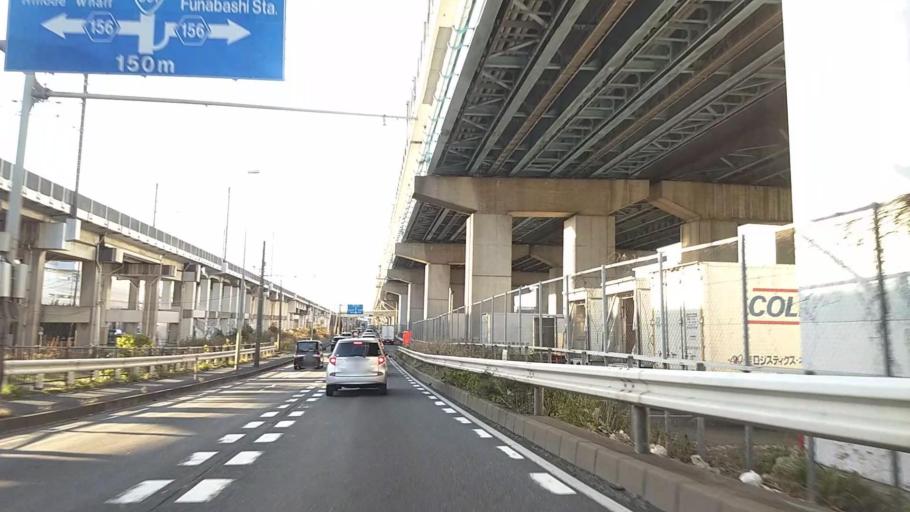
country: JP
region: Chiba
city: Funabashi
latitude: 35.6868
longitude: 139.9827
